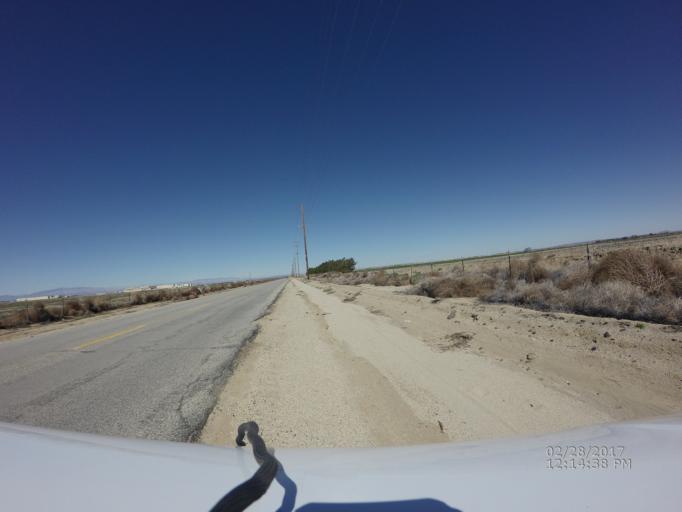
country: US
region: California
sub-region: Los Angeles County
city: Palmdale
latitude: 34.6203
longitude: -118.0586
